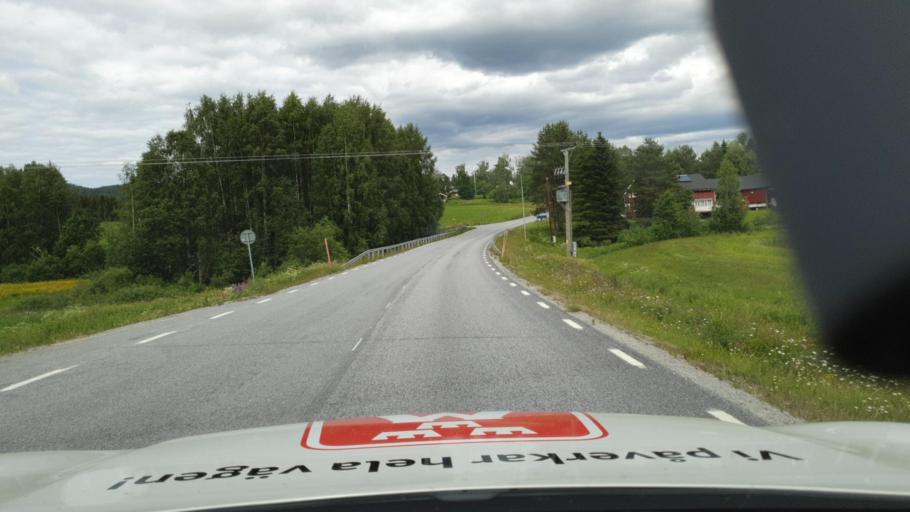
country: SE
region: Vaesterbotten
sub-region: Bjurholms Kommun
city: Bjurholm
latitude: 63.9132
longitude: 19.0883
